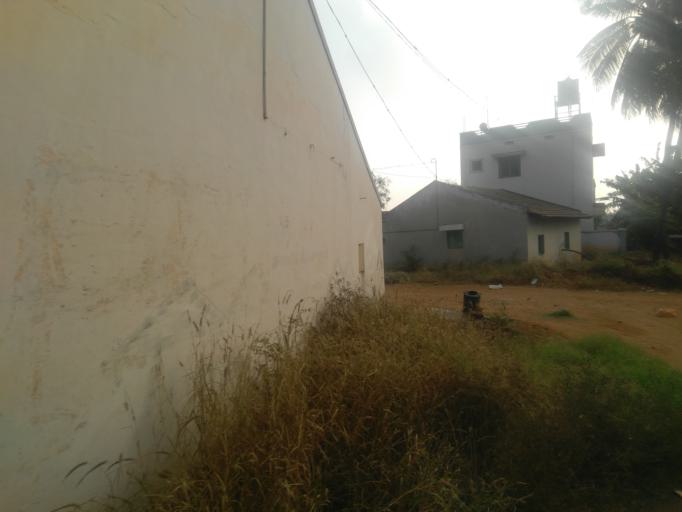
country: IN
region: Tamil Nadu
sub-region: Coimbatore
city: Perur
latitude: 11.0537
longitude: 76.8975
